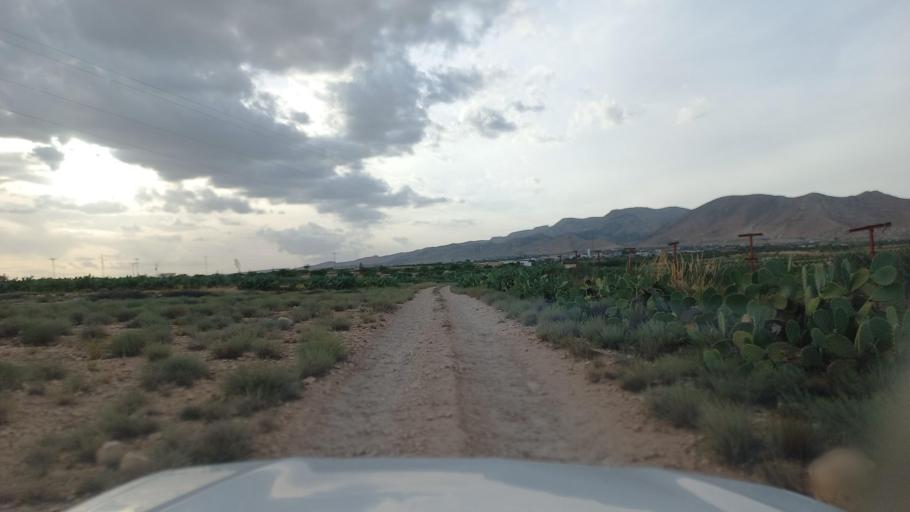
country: TN
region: Al Qasrayn
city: Sbiba
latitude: 35.4412
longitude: 9.0901
